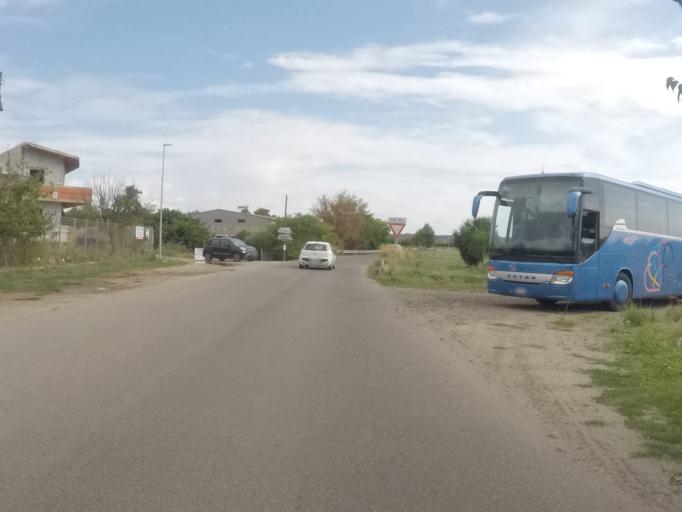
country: IT
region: Sardinia
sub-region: Provincia di Oristano
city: Bonarcado
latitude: 40.0911
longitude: 8.6565
